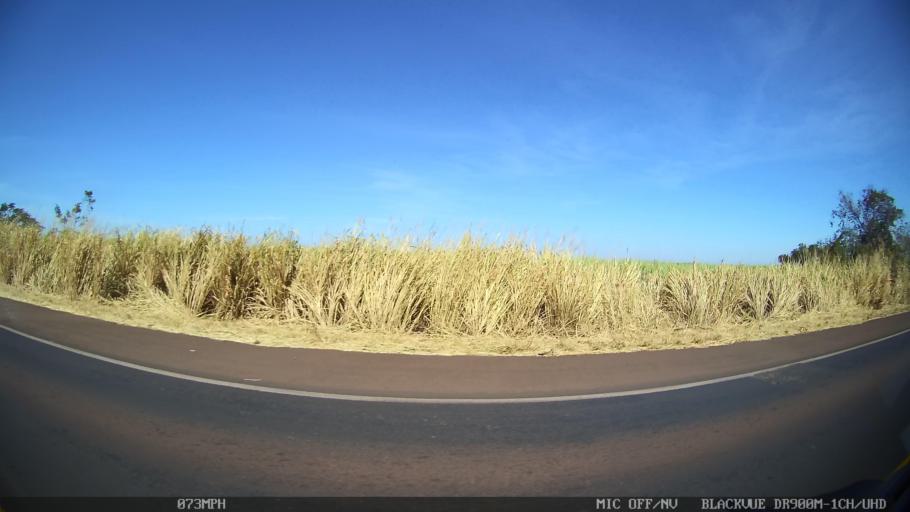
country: BR
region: Sao Paulo
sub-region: Barretos
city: Barretos
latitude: -20.4959
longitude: -48.5319
